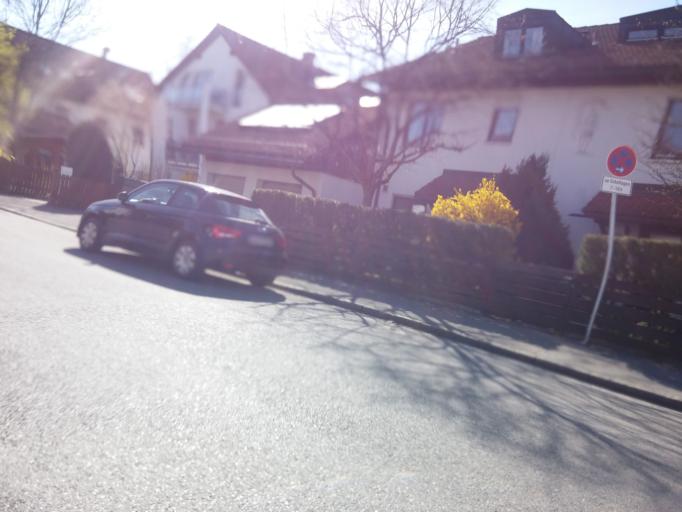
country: DE
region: Bavaria
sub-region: Upper Bavaria
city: Neubiberg
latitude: 48.0832
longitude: 11.6669
